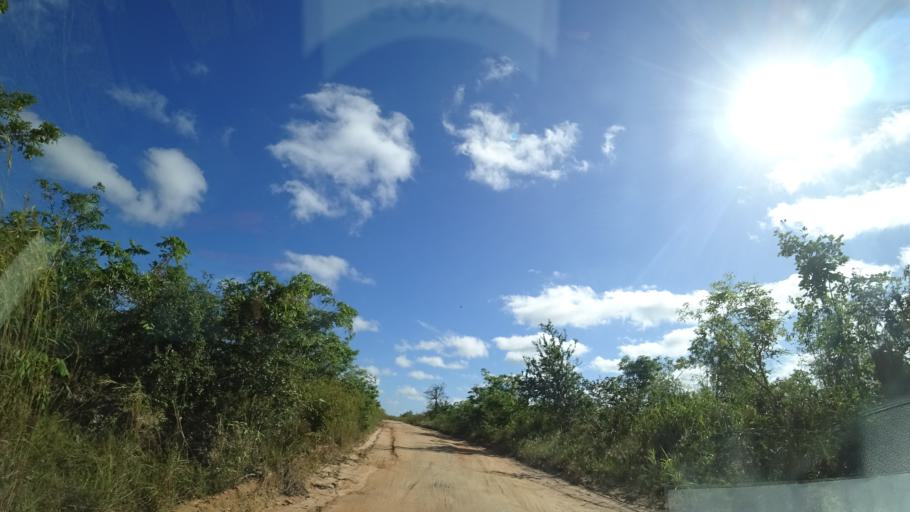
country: MZ
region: Sofala
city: Dondo
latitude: -19.4430
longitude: 34.7157
